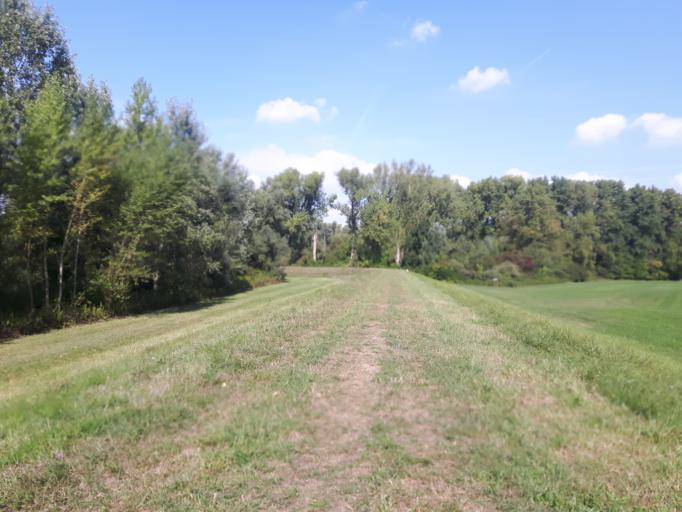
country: DE
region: Rheinland-Pfalz
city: Altrip
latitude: 49.3969
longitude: 8.4936
